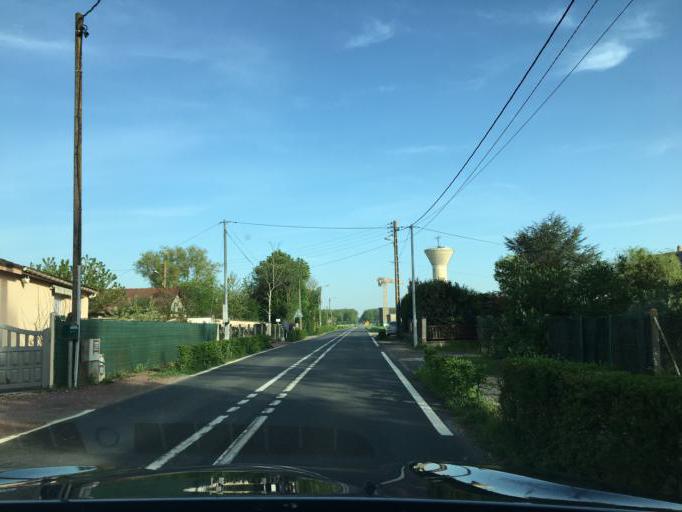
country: FR
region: Centre
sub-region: Departement d'Eure-et-Loir
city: Epernon
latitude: 48.6551
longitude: 1.6776
